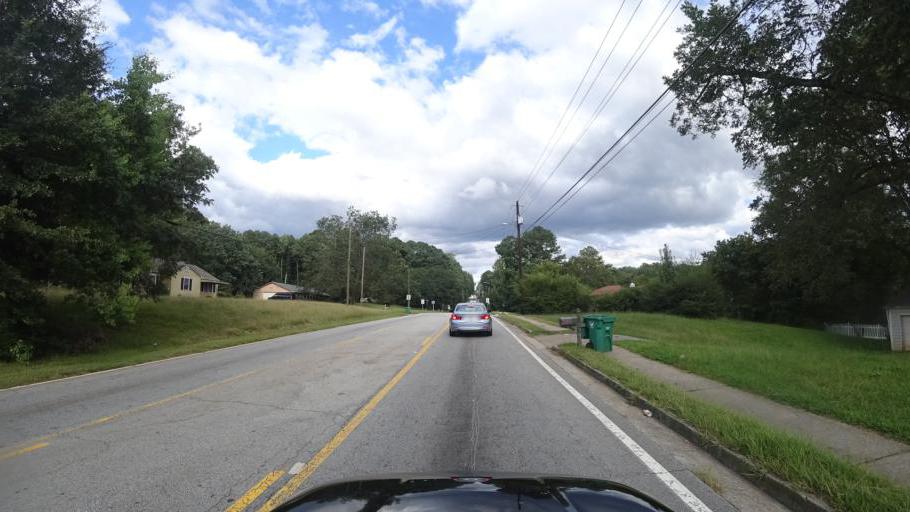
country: US
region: Georgia
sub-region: DeKalb County
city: Stone Mountain
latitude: 33.7598
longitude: -84.1843
